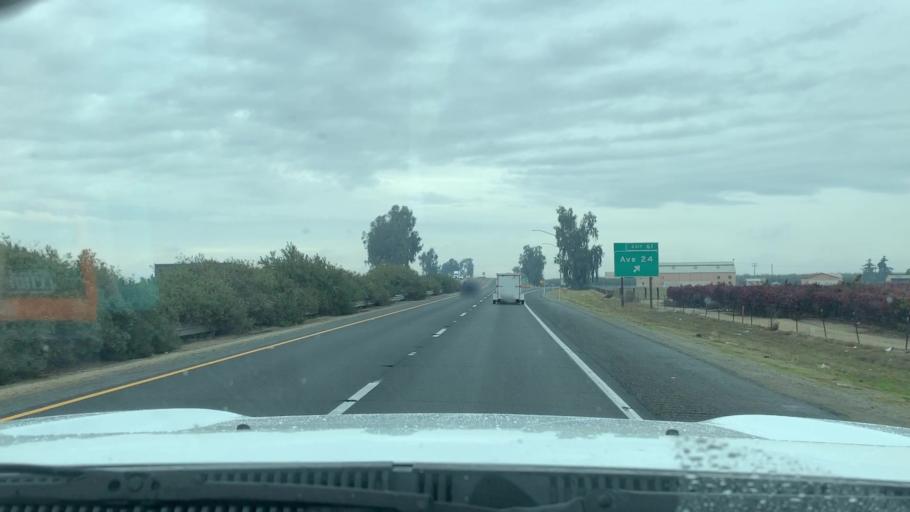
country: US
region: California
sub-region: Tulare County
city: Earlimart
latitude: 35.8294
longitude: -119.2593
